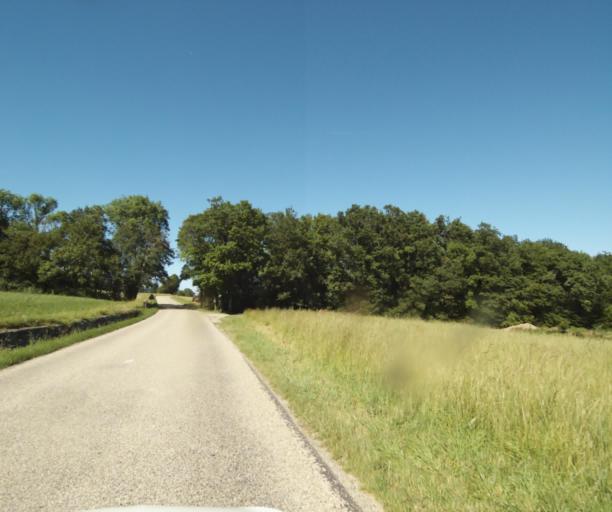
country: FR
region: Rhone-Alpes
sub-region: Departement de la Haute-Savoie
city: Sciez
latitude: 46.3016
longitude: 6.3781
